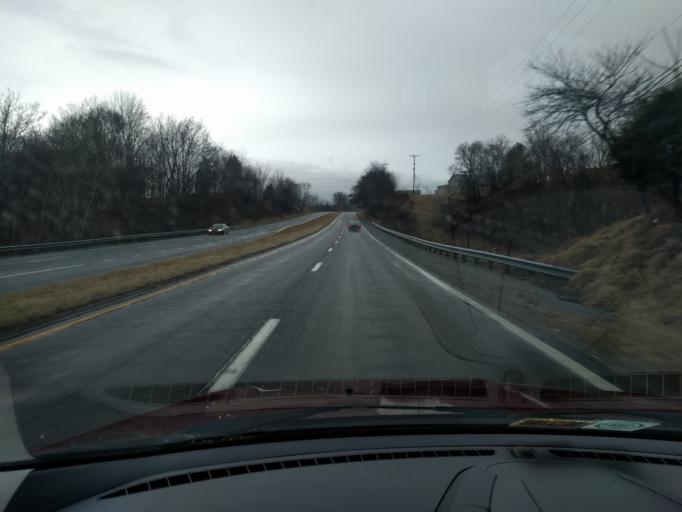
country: US
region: Virginia
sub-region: Giles County
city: Pembroke
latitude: 37.3007
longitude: -80.5623
